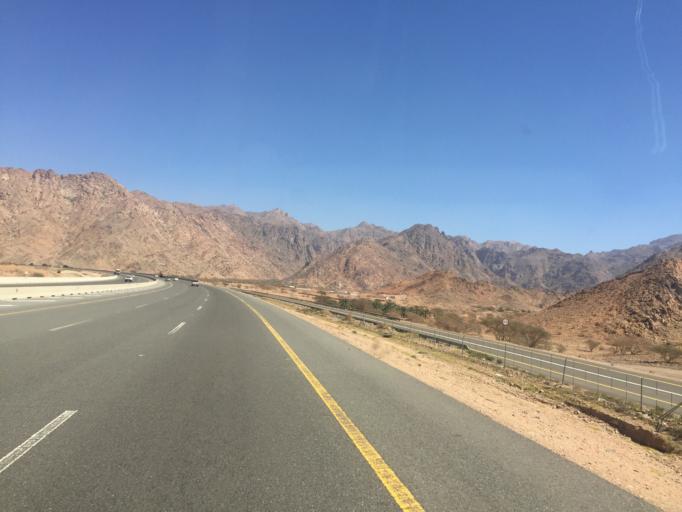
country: SA
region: Al Madinah al Munawwarah
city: Badr Hunayn
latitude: 24.0637
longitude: 39.2010
